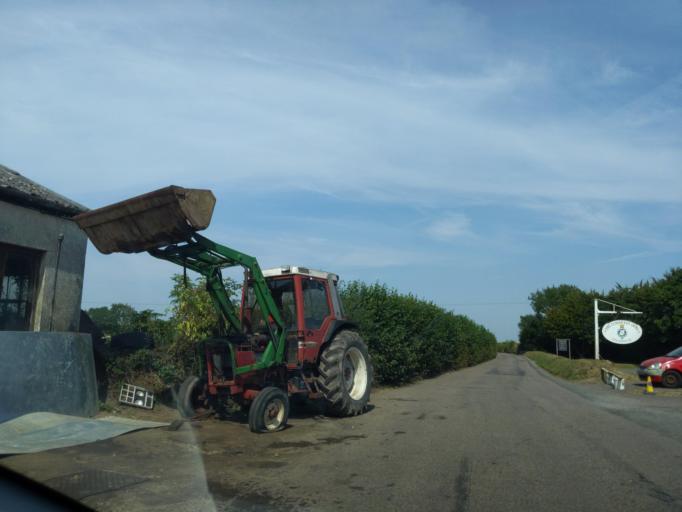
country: GB
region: England
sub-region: Devon
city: Winkleigh
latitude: 50.8668
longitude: -3.9004
